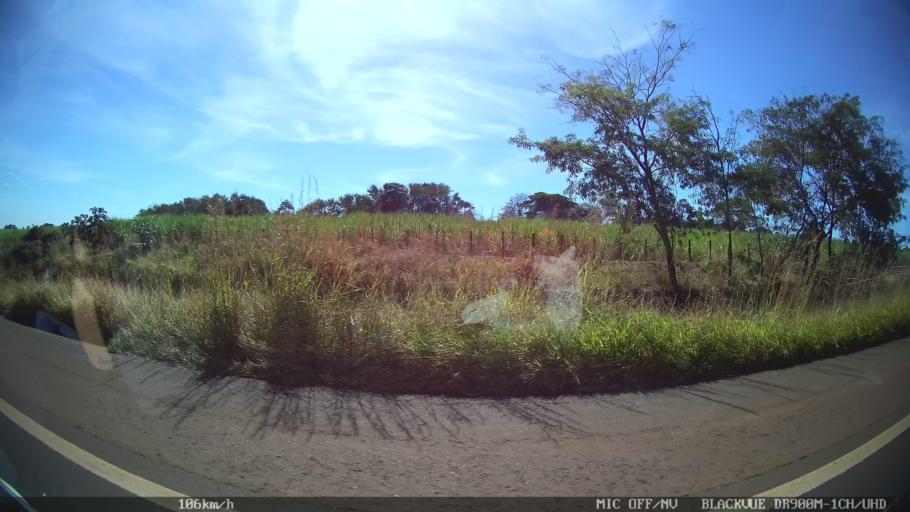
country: BR
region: Sao Paulo
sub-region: Franca
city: Franca
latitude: -20.5553
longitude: -47.5766
